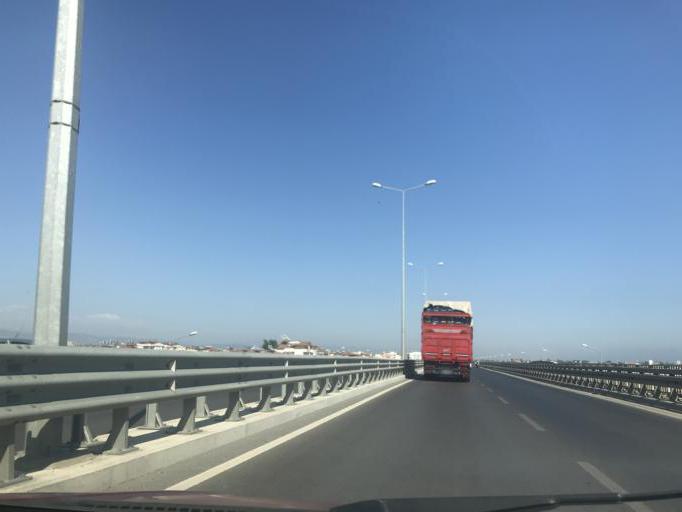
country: TR
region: Antalya
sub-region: Manavgat
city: Manavgat
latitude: 36.7803
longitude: 31.4299
